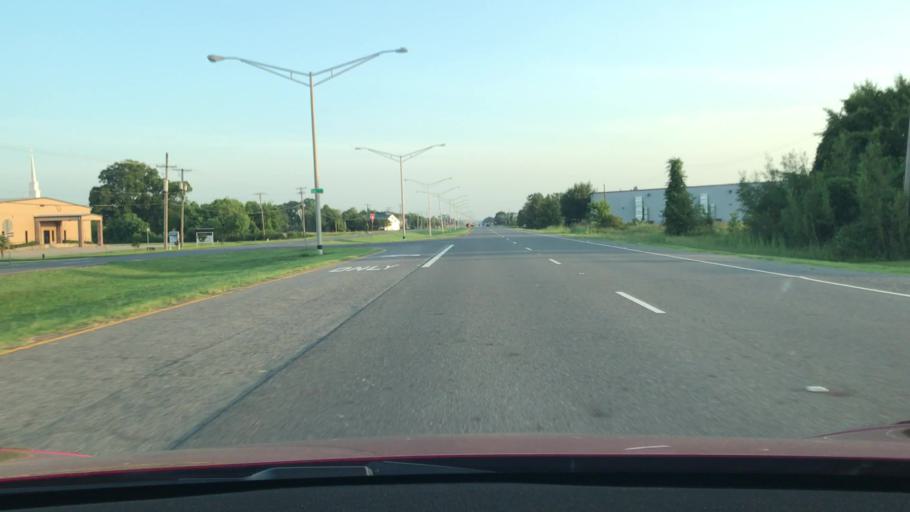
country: US
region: Louisiana
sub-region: Bossier Parish
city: Bossier City
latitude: 32.4051
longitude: -93.6963
